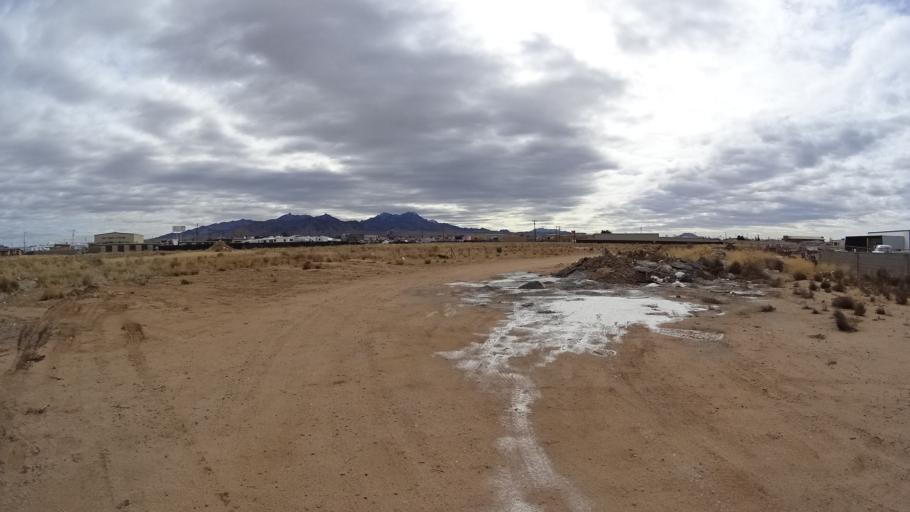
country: US
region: Arizona
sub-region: Mohave County
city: New Kingman-Butler
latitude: 35.2361
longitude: -113.9981
